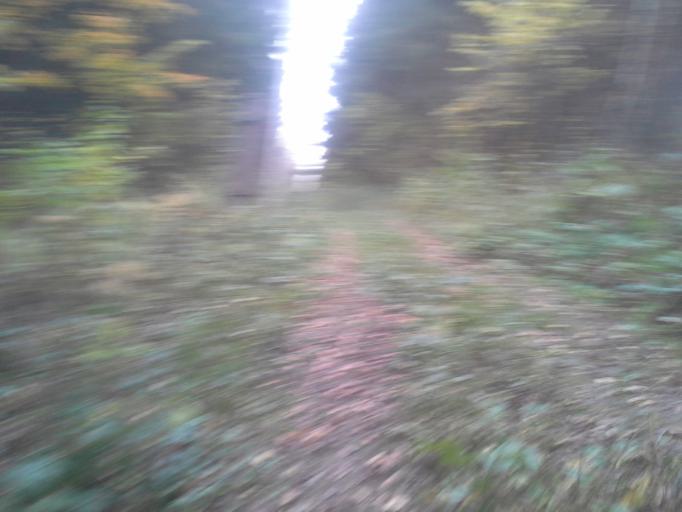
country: RU
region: Moskovskaya
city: Selyatino
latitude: 55.4632
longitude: 36.9744
